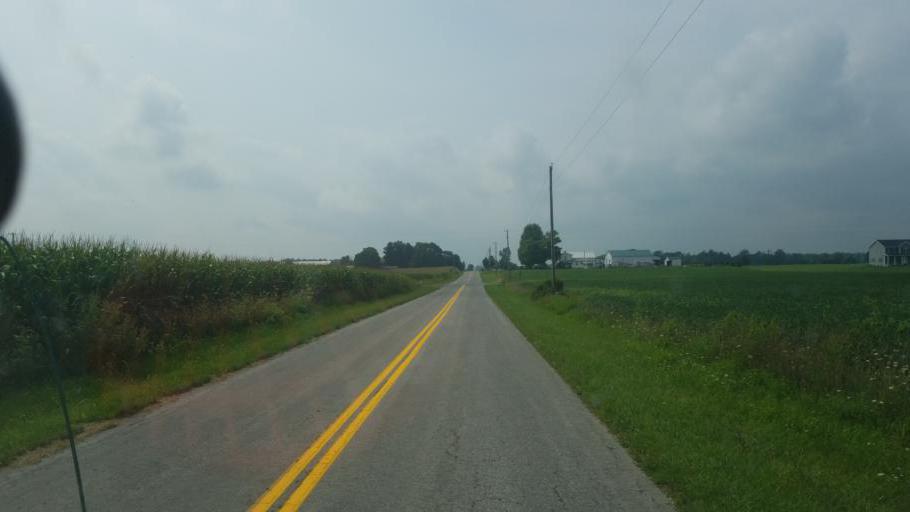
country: US
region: Ohio
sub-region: Huron County
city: Greenwich
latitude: 41.0523
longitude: -82.5596
